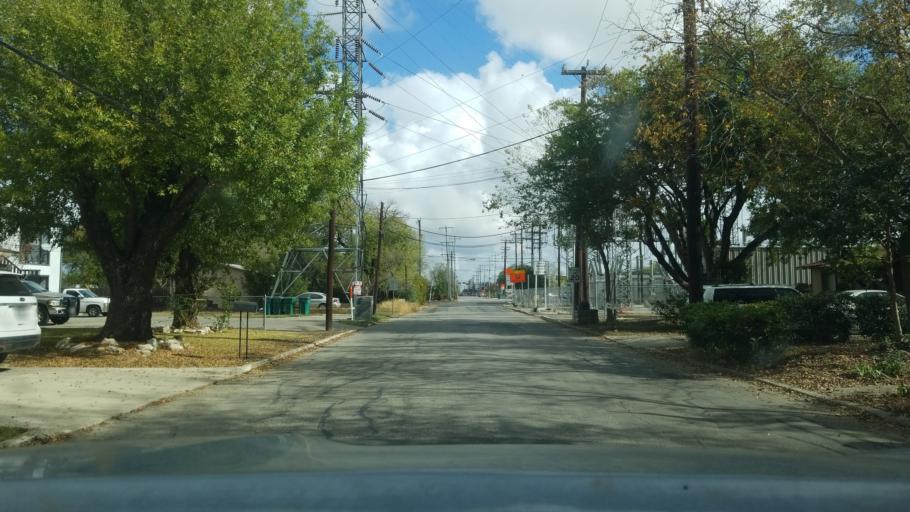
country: US
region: Texas
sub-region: Bexar County
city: Universal City
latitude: 29.5435
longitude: -98.2914
